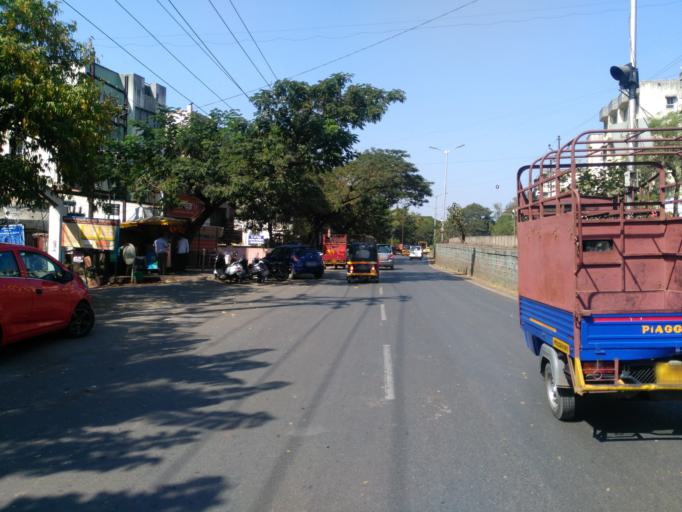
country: IN
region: Maharashtra
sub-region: Pune Division
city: Pune
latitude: 18.4725
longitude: 73.8630
